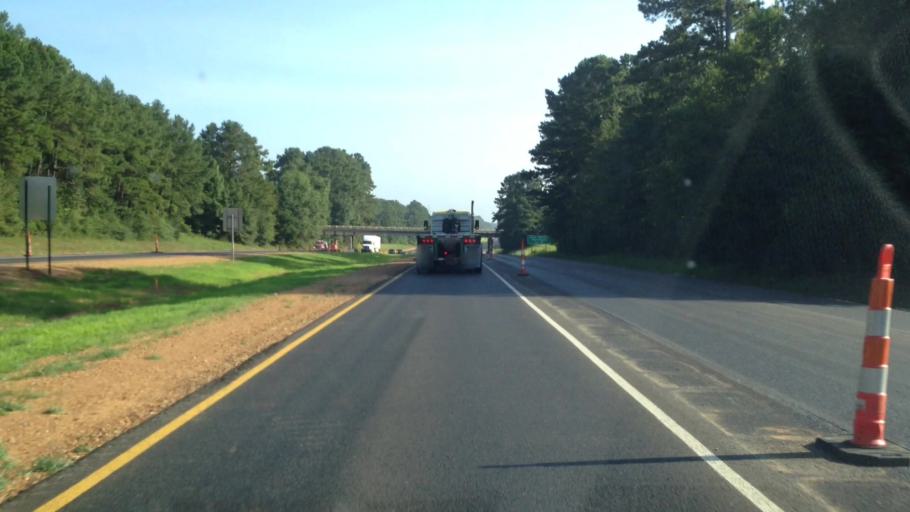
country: US
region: Mississippi
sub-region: Pike County
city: McComb
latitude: 31.2109
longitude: -90.4837
